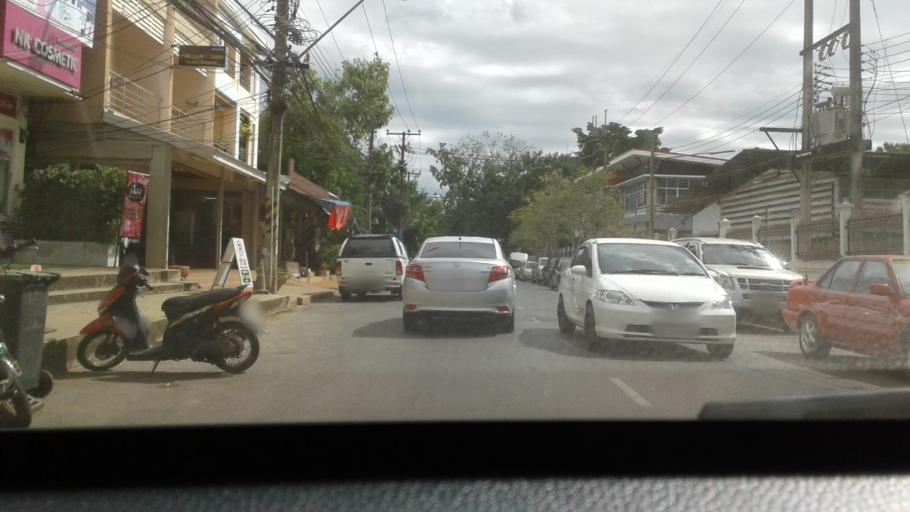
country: TH
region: Changwat Udon Thani
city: Udon Thani
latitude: 17.4171
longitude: 102.7894
